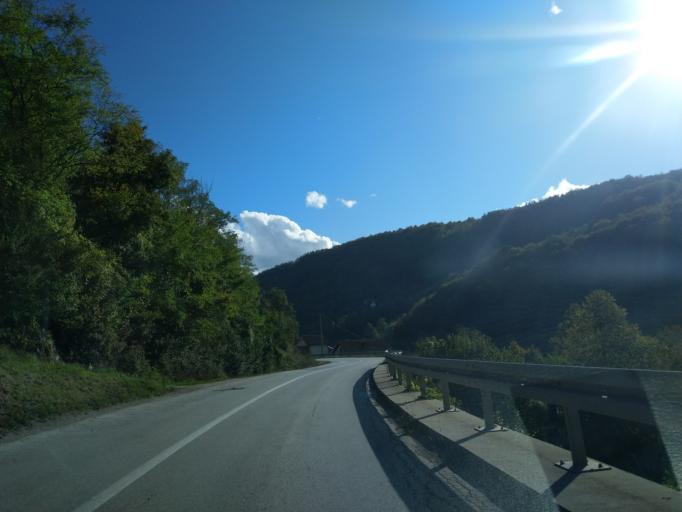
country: RS
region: Central Serbia
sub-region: Zlatiborski Okrug
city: Uzice
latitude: 43.8726
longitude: 19.7953
